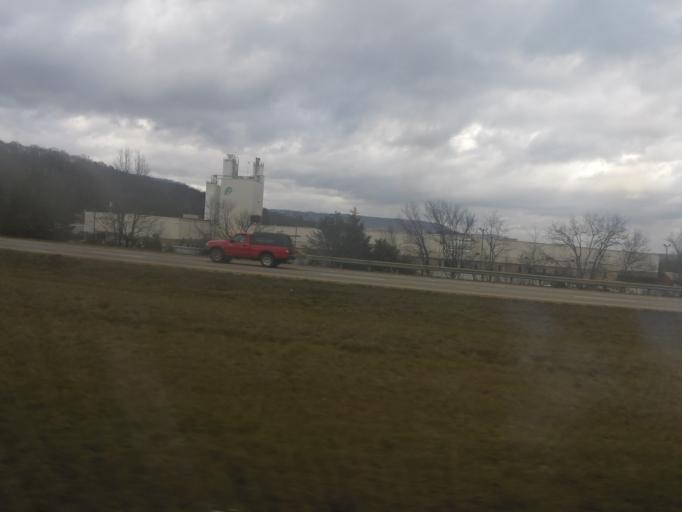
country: US
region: Tennessee
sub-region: Marion County
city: Jasper
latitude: 35.0505
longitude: -85.6370
